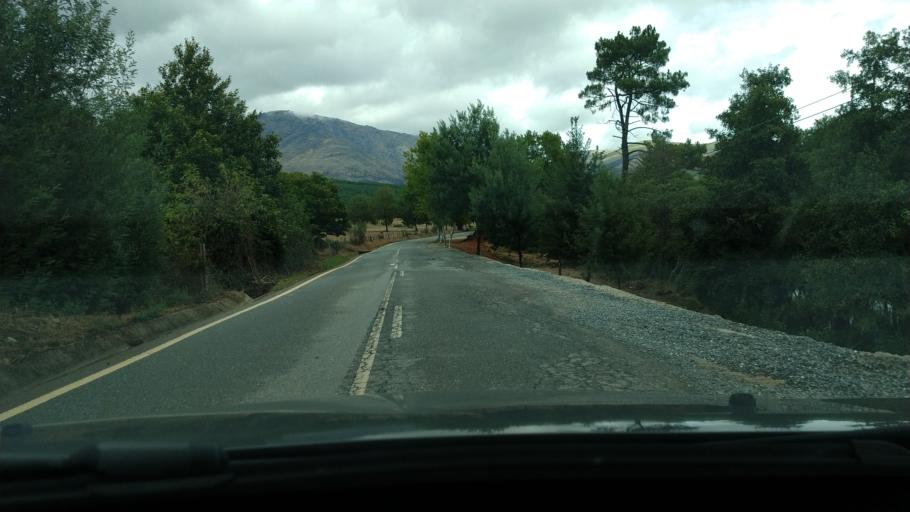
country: PT
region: Castelo Branco
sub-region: Covilha
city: Covilha
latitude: 40.2290
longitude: -7.6069
